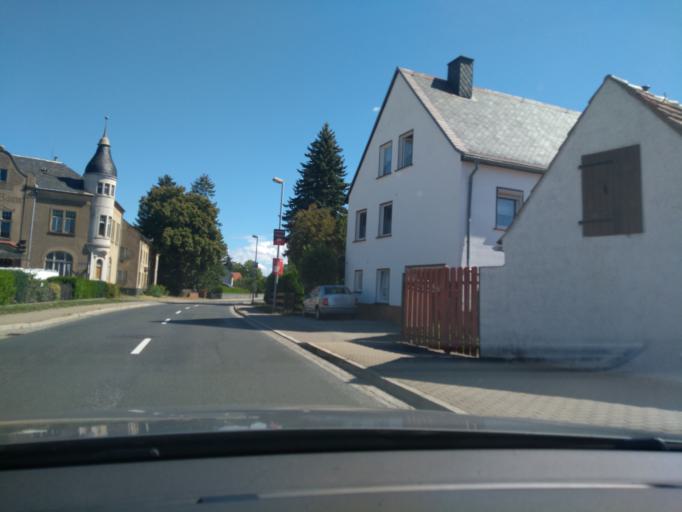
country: DE
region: Saxony
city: Grossrohrsdorf
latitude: 51.1454
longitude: 14.0291
